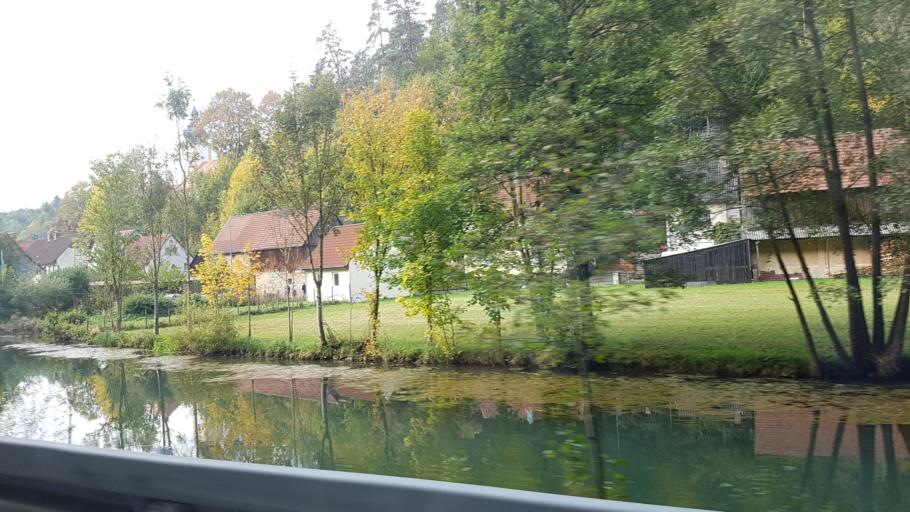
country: DE
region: Bavaria
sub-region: Upper Franconia
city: Plankenfels
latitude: 49.8670
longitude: 11.3387
